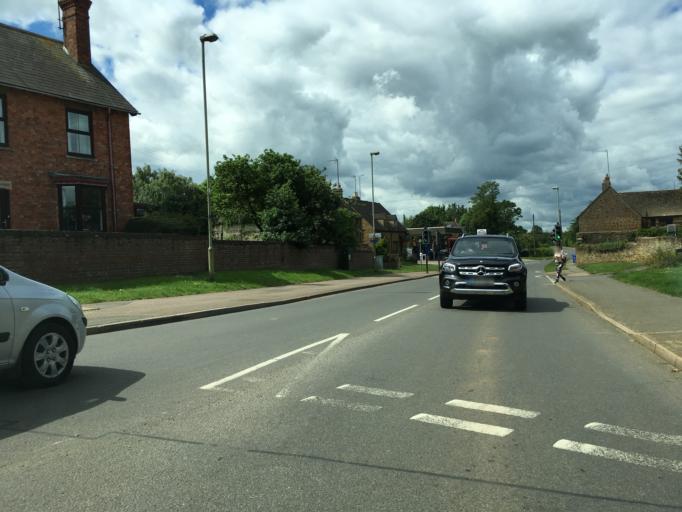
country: GB
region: England
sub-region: Oxfordshire
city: Bloxham
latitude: 52.0161
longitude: -1.3762
